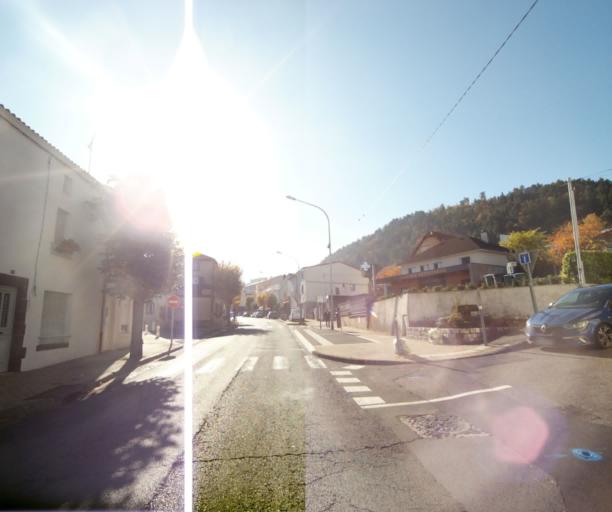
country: FR
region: Auvergne
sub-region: Departement du Puy-de-Dome
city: Ceyrat
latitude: 45.7326
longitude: 3.0637
